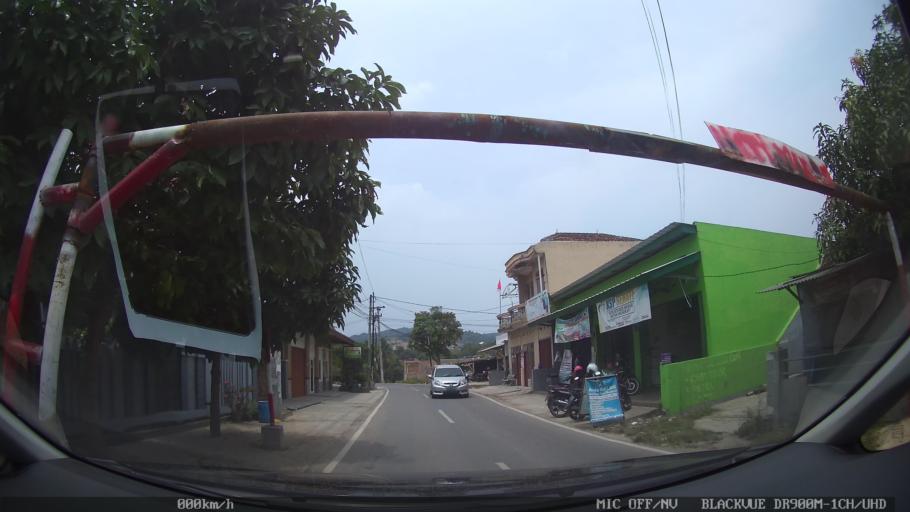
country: ID
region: Lampung
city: Kedaton
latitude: -5.3973
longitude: 105.3159
